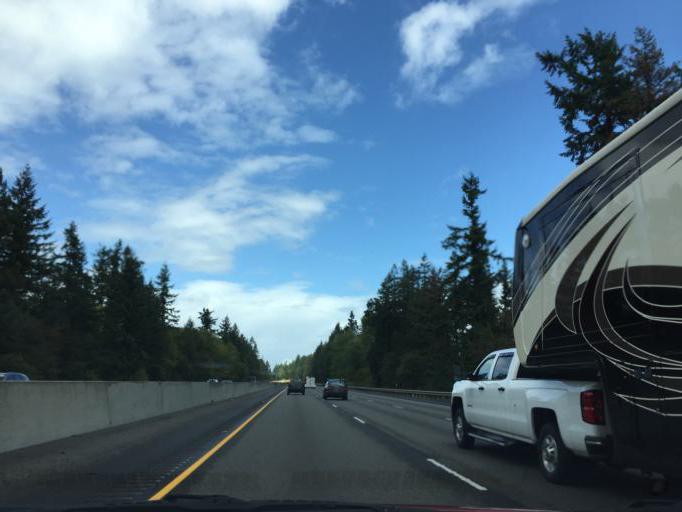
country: US
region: Washington
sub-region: Thurston County
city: Grand Mound
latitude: 46.8530
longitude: -122.9769
